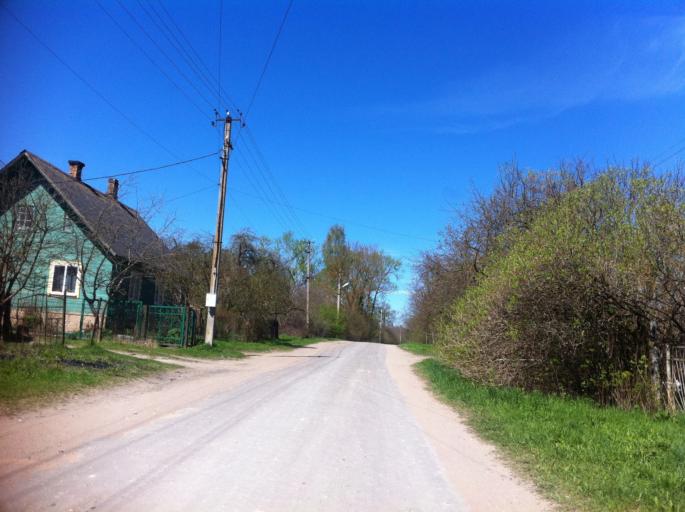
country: RU
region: Pskov
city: Izborsk
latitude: 57.7758
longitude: 27.9677
